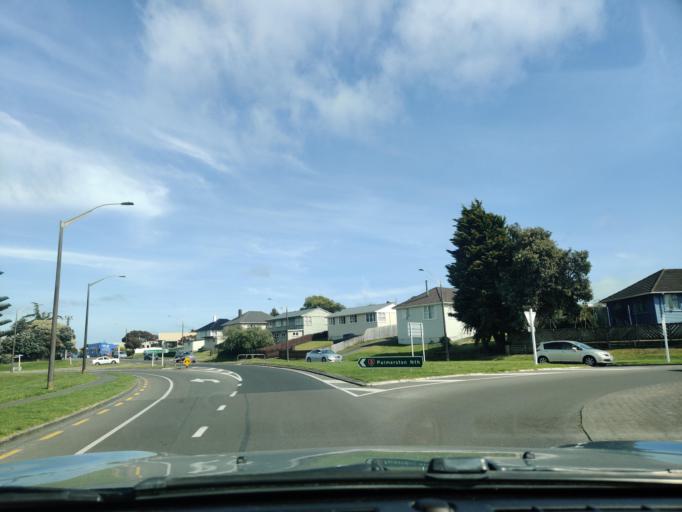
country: NZ
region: Manawatu-Wanganui
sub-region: Wanganui District
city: Wanganui
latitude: -39.9329
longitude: 175.0289
